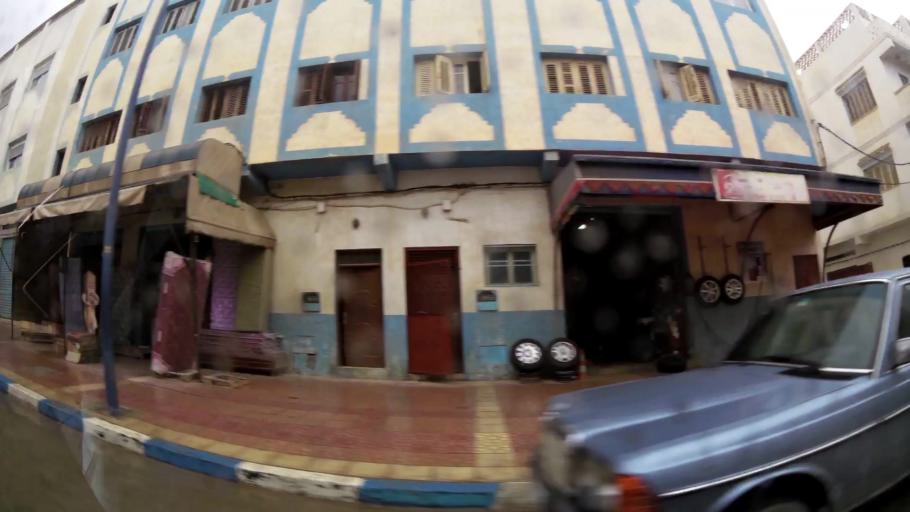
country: MA
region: Taza-Al Hoceima-Taounate
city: Imzourene
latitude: 35.1410
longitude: -3.8547
